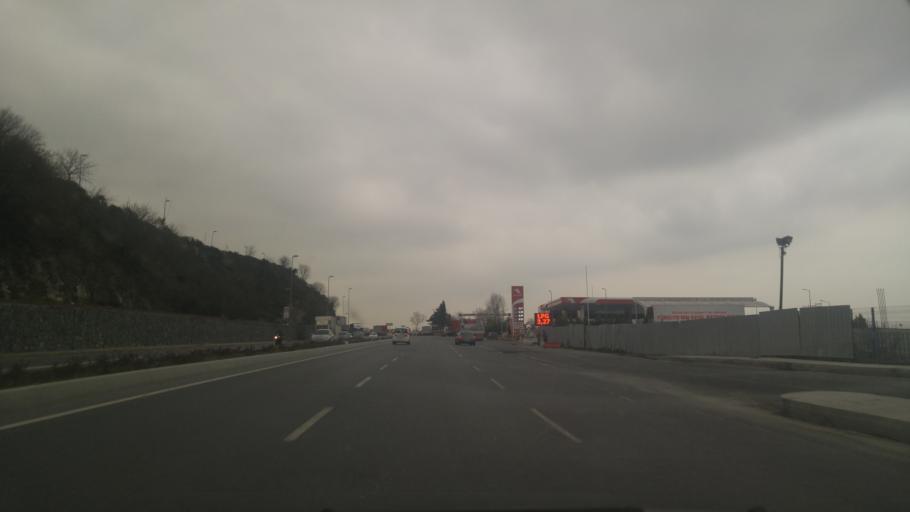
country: TR
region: Istanbul
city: Mahmutbey
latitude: 41.0155
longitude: 28.7686
